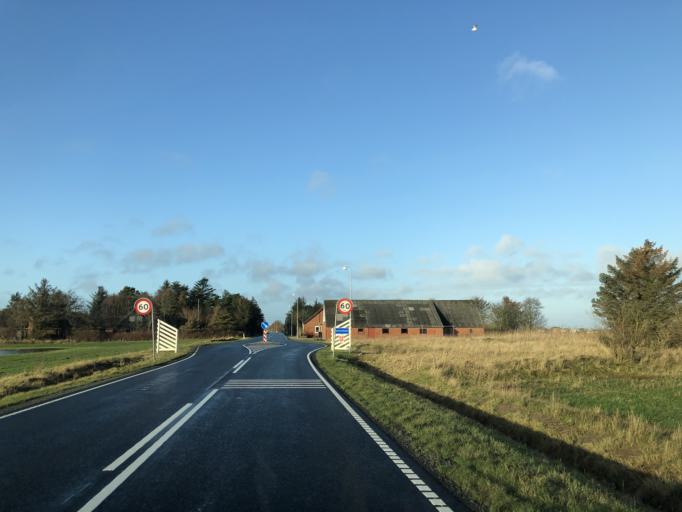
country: DK
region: Central Jutland
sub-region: Struer Kommune
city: Struer
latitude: 56.5445
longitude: 8.4986
